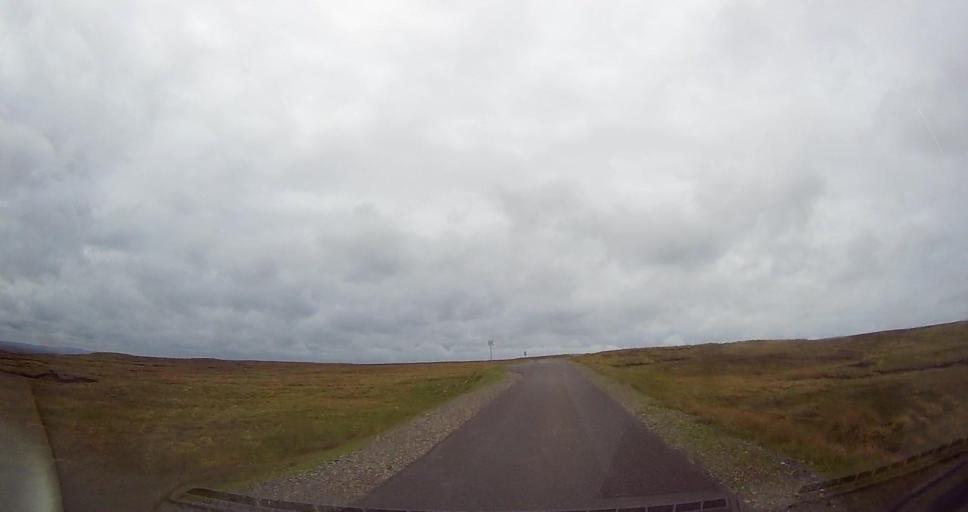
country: GB
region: Scotland
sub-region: Shetland Islands
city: Lerwick
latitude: 60.4916
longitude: -1.5810
